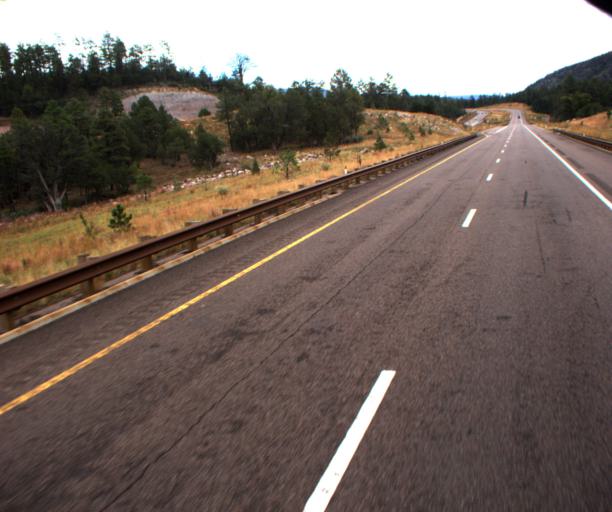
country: US
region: Arizona
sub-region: Gila County
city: Star Valley
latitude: 34.3128
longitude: -111.0533
